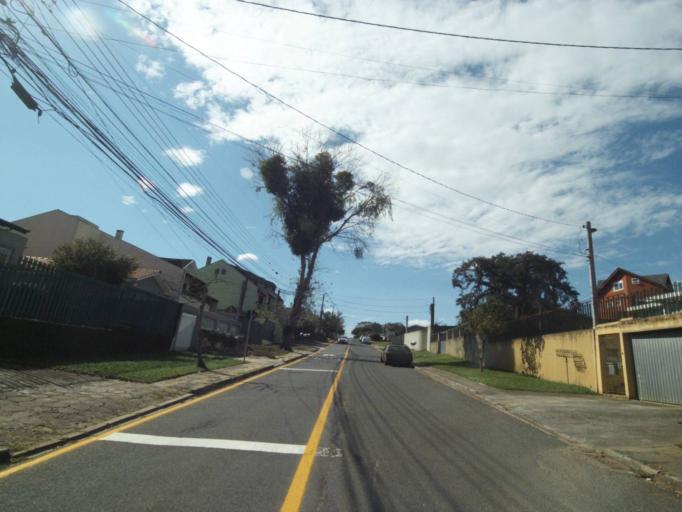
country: BR
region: Parana
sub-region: Curitiba
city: Curitiba
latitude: -25.4101
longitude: -49.2785
